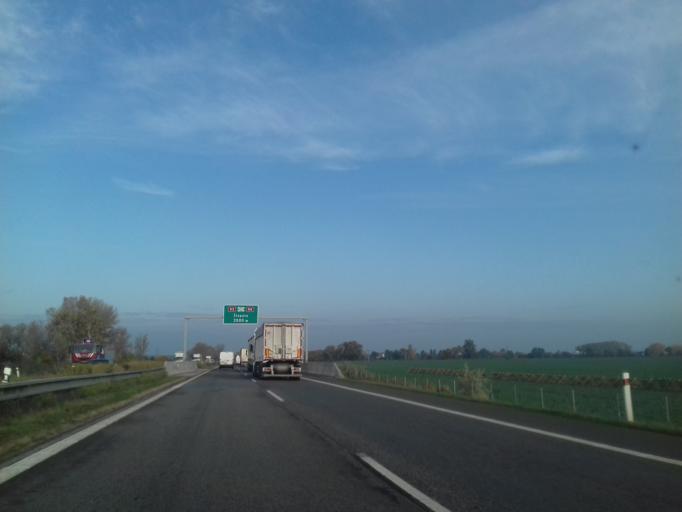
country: SK
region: Bratislavsky
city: Stupava
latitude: 48.2278
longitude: 17.0240
